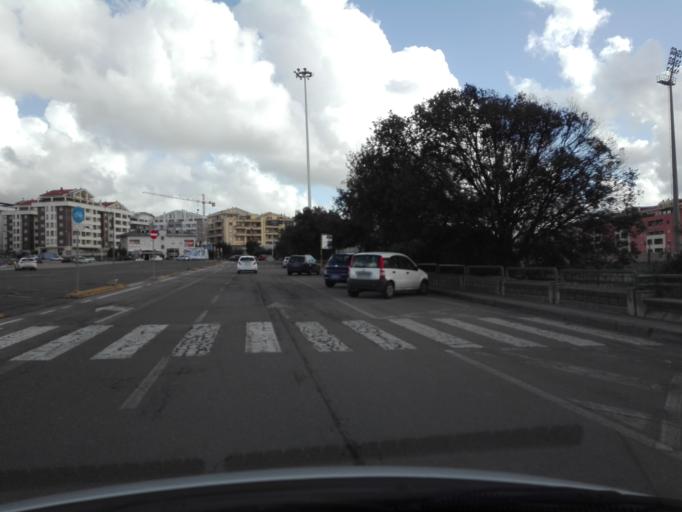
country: IT
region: Sardinia
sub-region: Provincia di Sassari
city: Sassari
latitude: 40.7182
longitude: 8.5815
